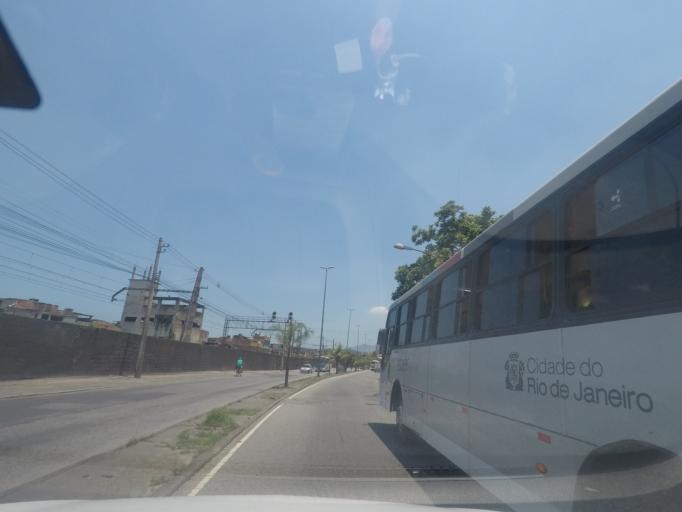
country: BR
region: Rio de Janeiro
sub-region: Duque De Caxias
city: Duque de Caxias
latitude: -22.8106
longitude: -43.3016
